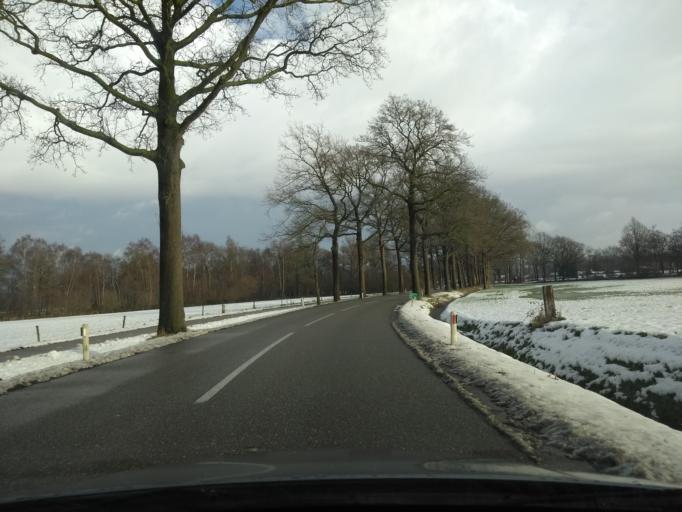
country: NL
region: Gelderland
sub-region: Berkelland
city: Borculo
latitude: 52.1111
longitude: 6.5685
